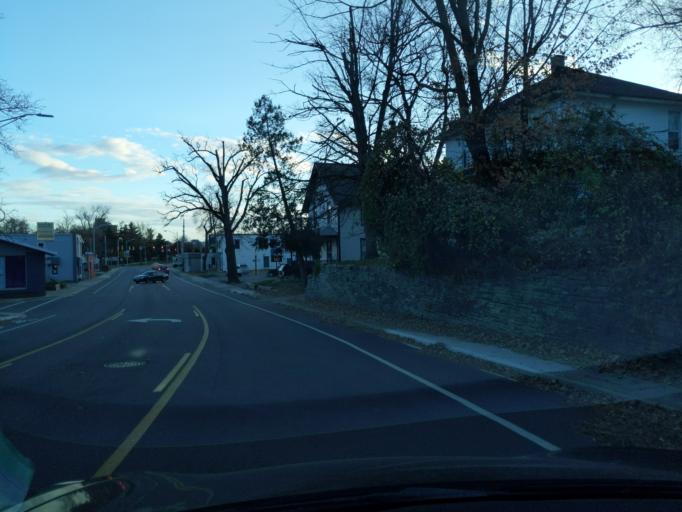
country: US
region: Michigan
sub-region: Ingham County
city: East Lansing
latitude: 42.7353
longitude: -84.4935
